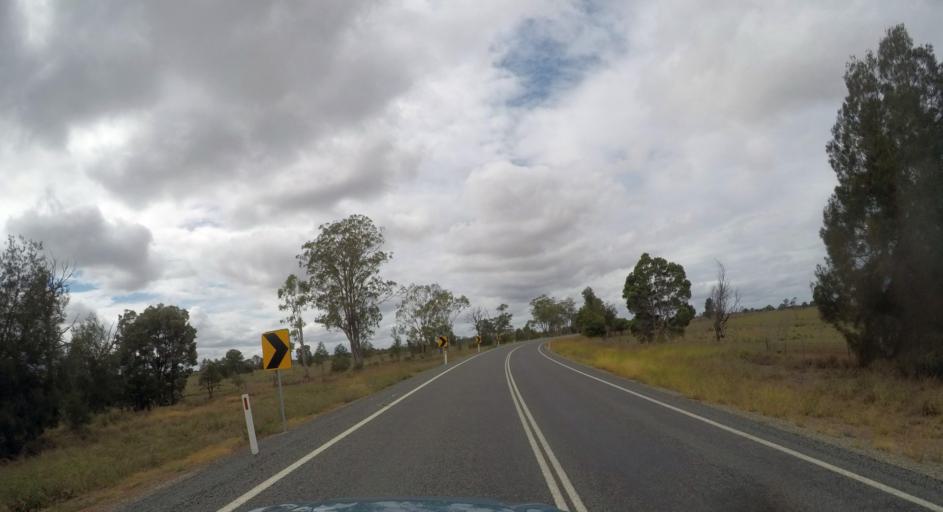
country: AU
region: Queensland
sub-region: South Burnett
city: Kingaroy
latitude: -26.3903
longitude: 151.2017
